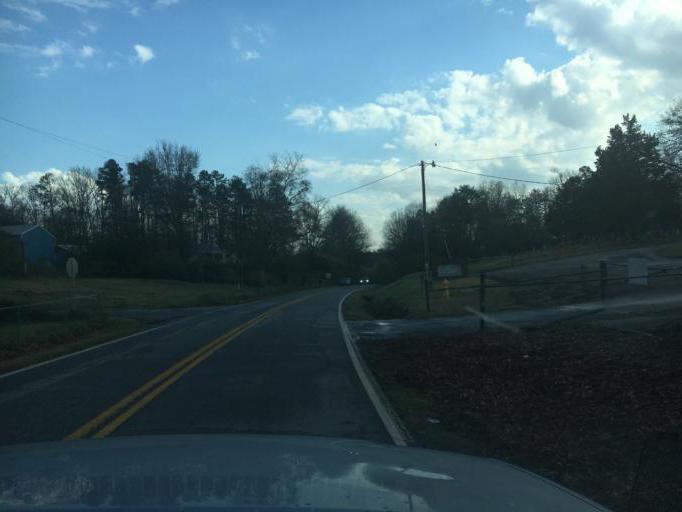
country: US
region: South Carolina
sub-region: Greenville County
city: Parker
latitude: 34.8437
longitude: -82.4942
